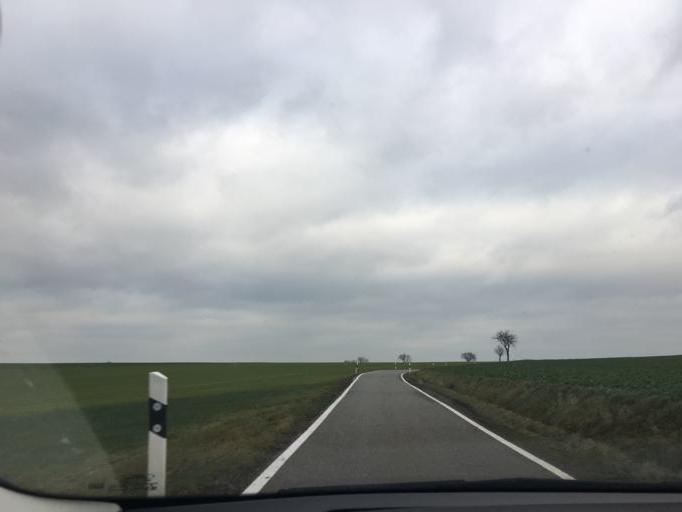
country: DE
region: Saxony
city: Niederfrohna
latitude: 50.8595
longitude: 12.7060
